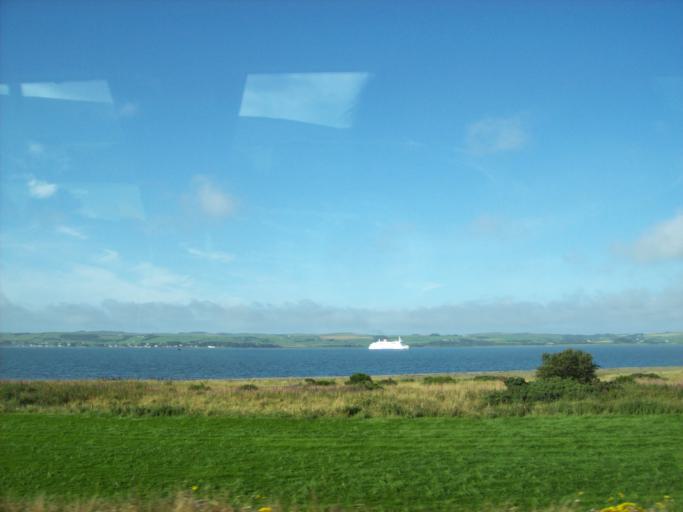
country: GB
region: Scotland
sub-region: Dumfries and Galloway
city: Cairnryan
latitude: 54.9411
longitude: -4.9989
